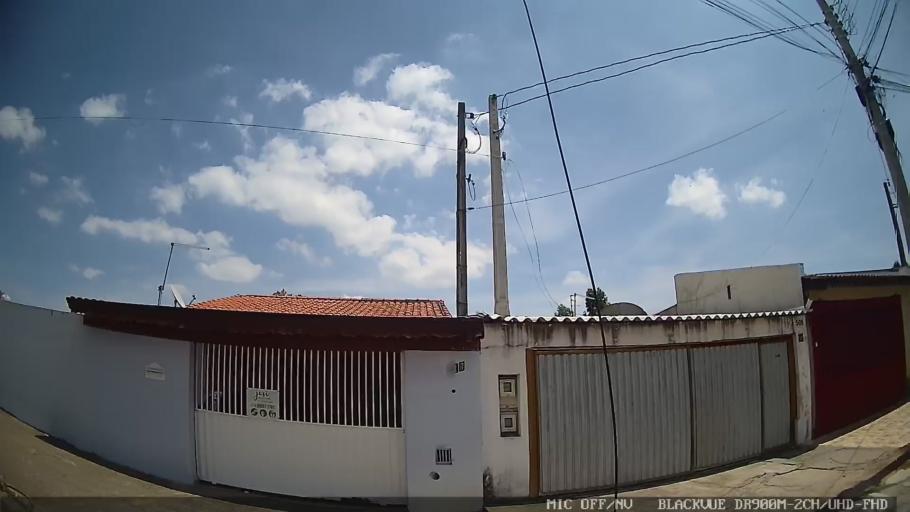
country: BR
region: Sao Paulo
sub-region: Cabreuva
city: Cabreuva
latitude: -23.2605
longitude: -47.0544
